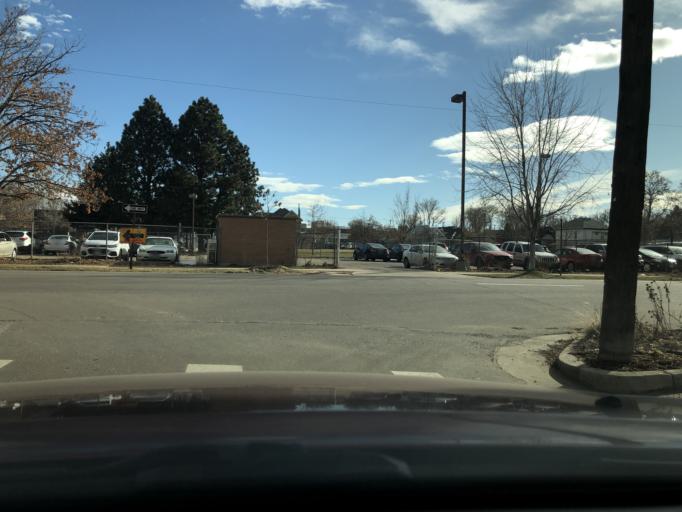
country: US
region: Colorado
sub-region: Denver County
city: Denver
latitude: 39.7581
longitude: -104.9775
